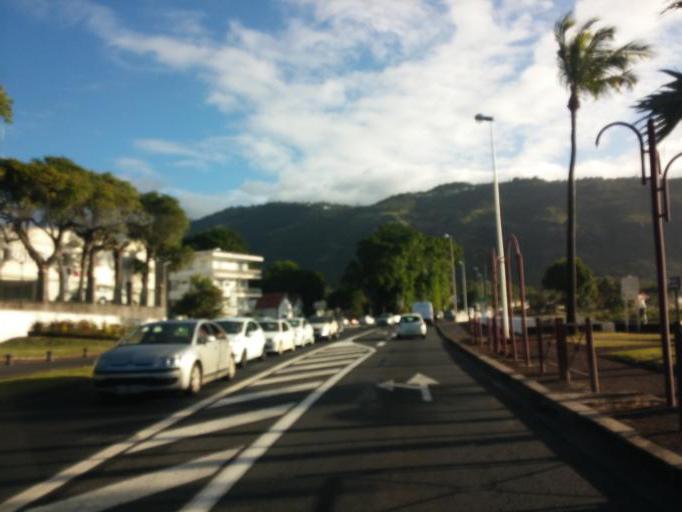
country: RE
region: Reunion
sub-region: Reunion
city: Saint-Denis
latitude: -20.8750
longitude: 55.4459
